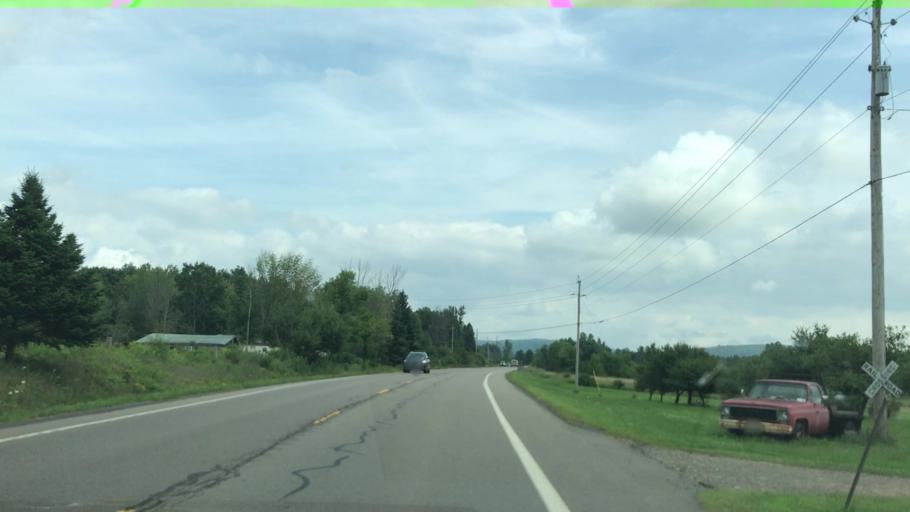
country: US
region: New York
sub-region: Steuben County
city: Bath
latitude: 42.4690
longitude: -77.2990
